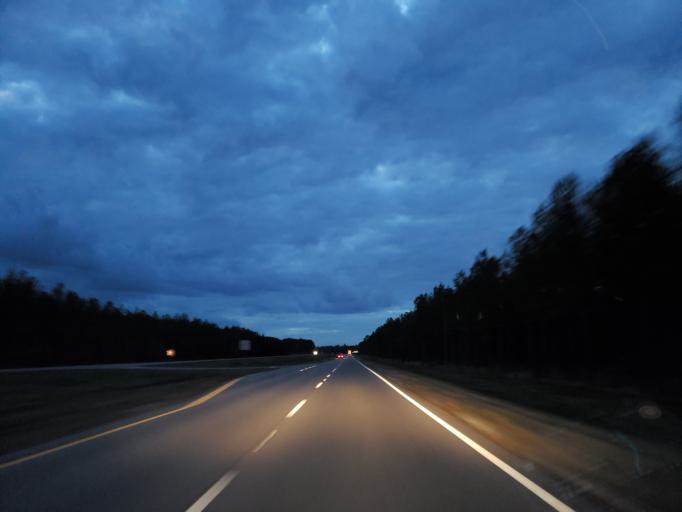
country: US
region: Mississippi
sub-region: Forrest County
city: Hattiesburg
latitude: 31.2421
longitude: -89.2222
